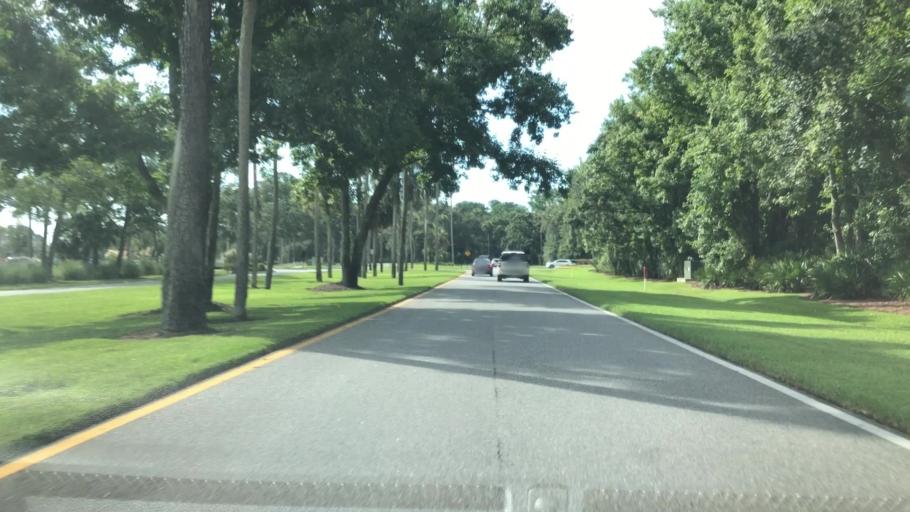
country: US
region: Florida
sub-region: Saint Johns County
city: Sawgrass
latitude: 30.2046
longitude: -81.3840
